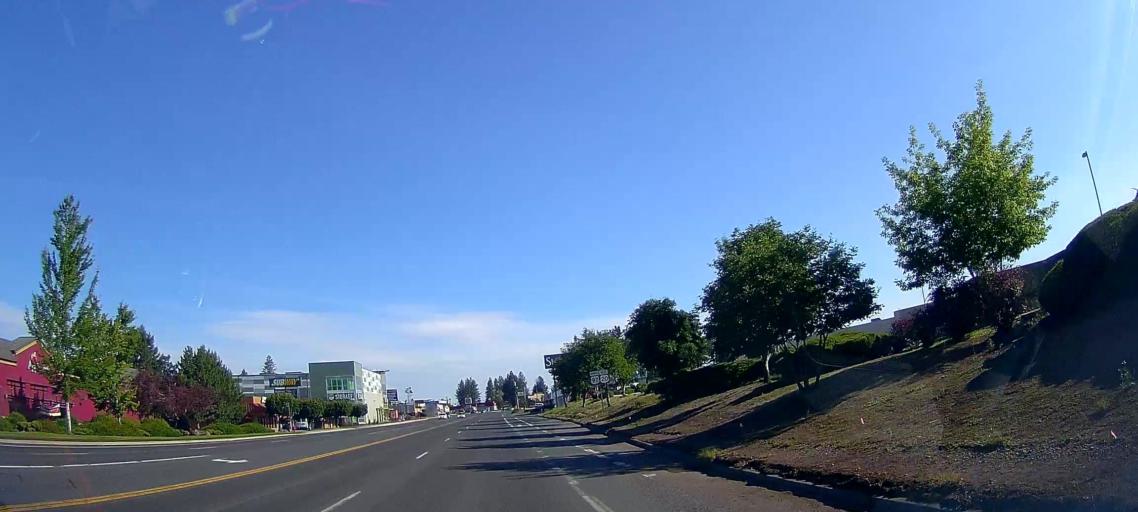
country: US
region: Oregon
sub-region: Deschutes County
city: Bend
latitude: 44.0840
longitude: -121.3056
